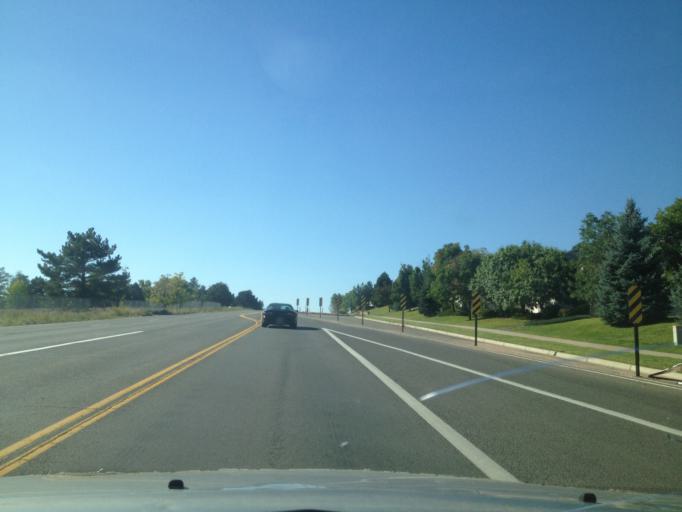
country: US
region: Colorado
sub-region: Jefferson County
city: Applewood
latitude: 39.8061
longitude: -105.1747
